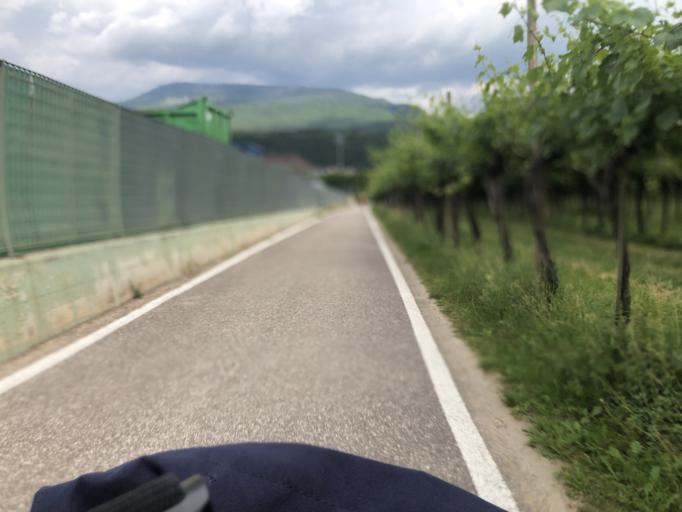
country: IT
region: Trentino-Alto Adige
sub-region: Provincia di Trento
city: Nogaredo
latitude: 45.9025
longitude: 11.0320
